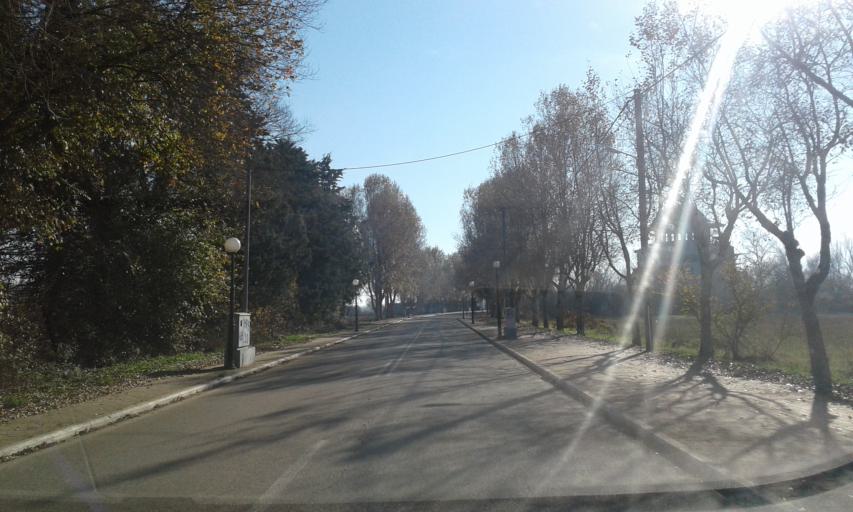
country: GR
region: Central Macedonia
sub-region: Nomos Thessalonikis
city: Lagkadas
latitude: 40.7401
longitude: 23.0797
